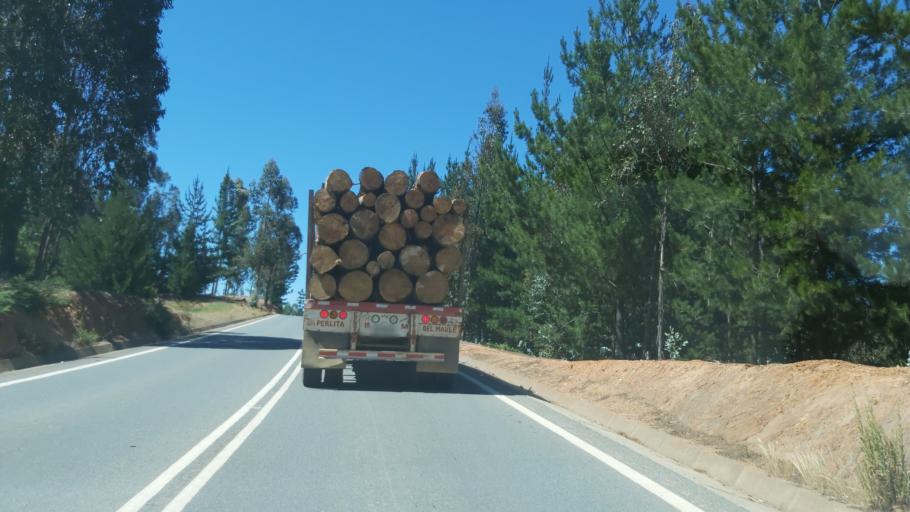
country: CL
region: Maule
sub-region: Provincia de Talca
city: Constitucion
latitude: -34.9323
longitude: -71.9865
